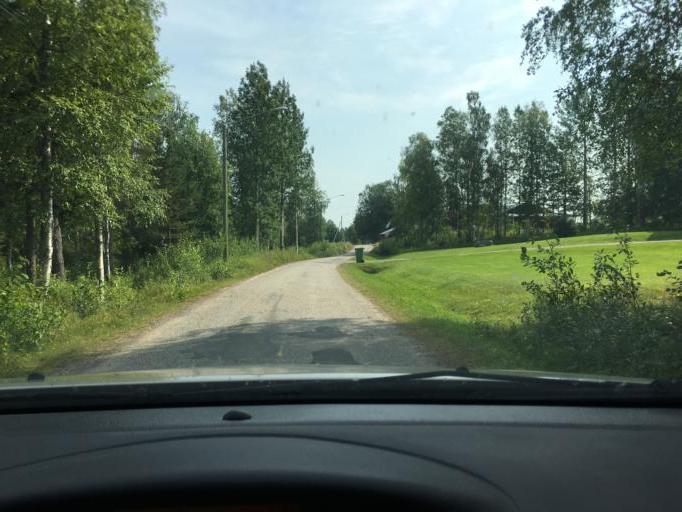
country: SE
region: Norrbotten
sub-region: Kalix Kommun
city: Rolfs
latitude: 65.7654
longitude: 23.0078
